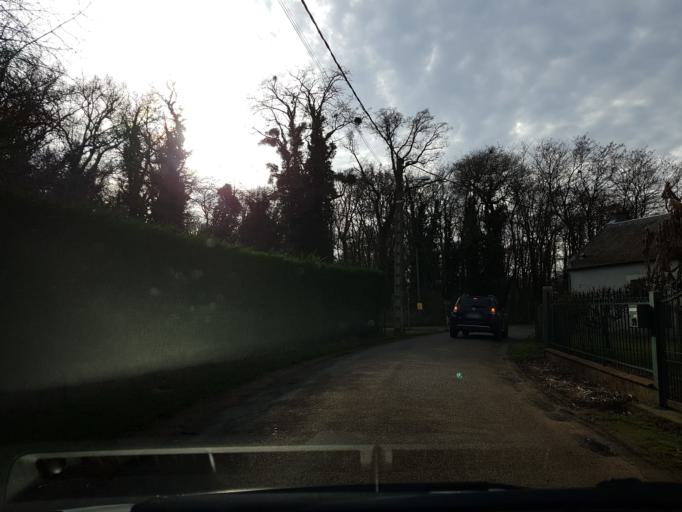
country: FR
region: Centre
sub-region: Departement du Loiret
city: Saint-Denis-en-Val
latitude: 47.8873
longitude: 1.9679
